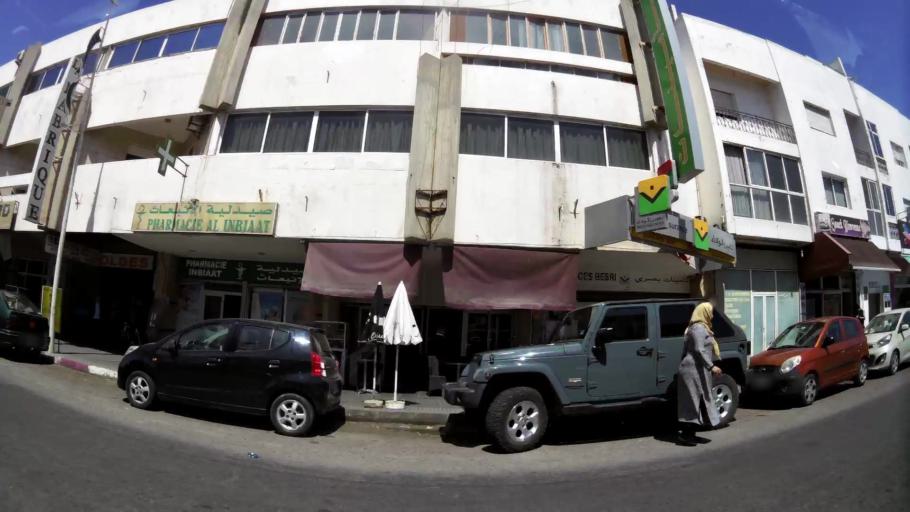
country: MA
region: Souss-Massa-Draa
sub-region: Agadir-Ida-ou-Tnan
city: Agadir
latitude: 30.4137
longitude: -9.5928
